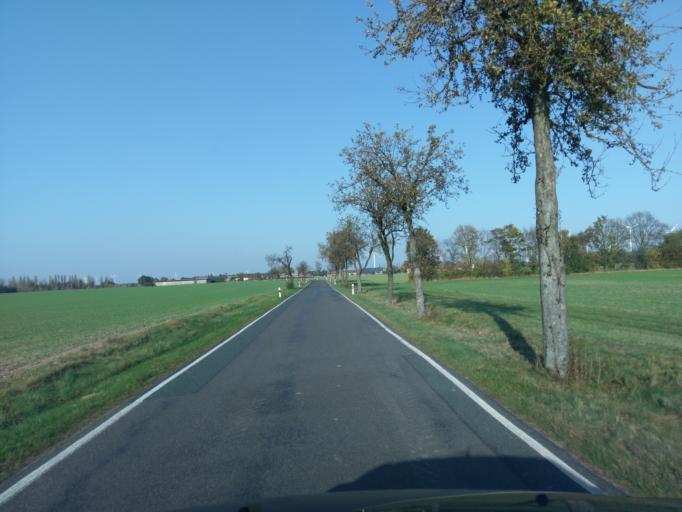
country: DE
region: Brandenburg
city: Falkenberg
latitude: 51.5097
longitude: 13.2940
